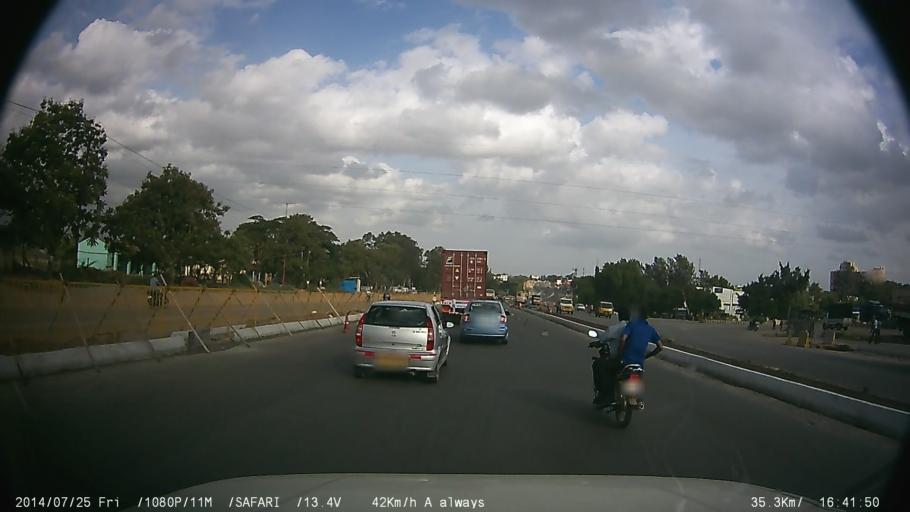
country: IN
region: Tamil Nadu
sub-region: Krishnagiri
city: Hosur
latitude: 12.7587
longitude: 77.7984
